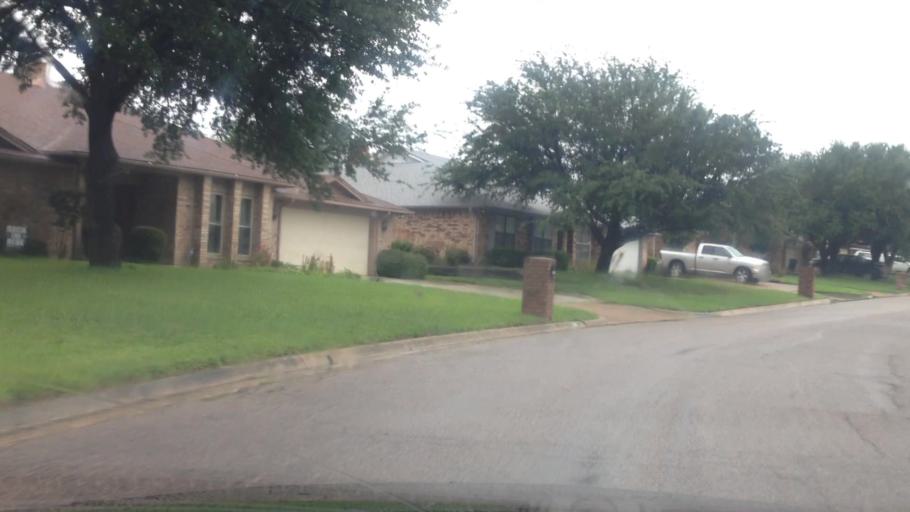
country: US
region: Texas
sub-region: Tarrant County
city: Watauga
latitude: 32.8813
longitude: -97.2282
